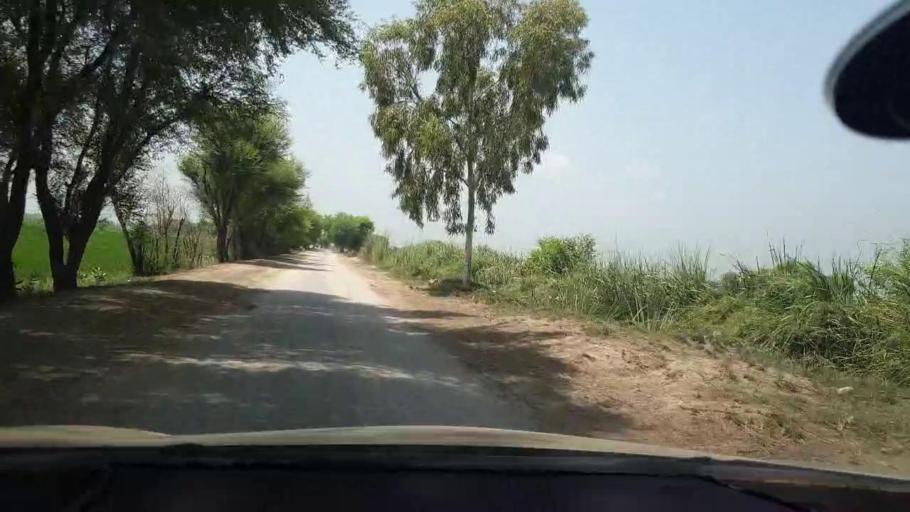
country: PK
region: Sindh
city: Kambar
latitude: 27.6640
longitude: 67.9250
